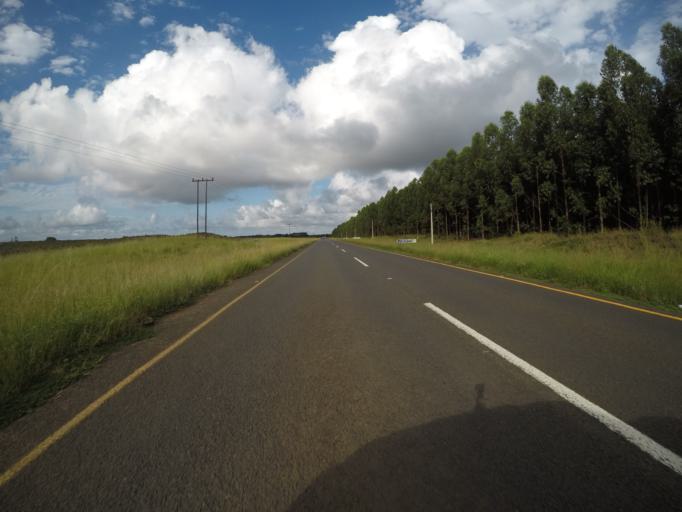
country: ZA
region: KwaZulu-Natal
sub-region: uMkhanyakude District Municipality
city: Mtubatuba
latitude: -28.3843
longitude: 32.2392
